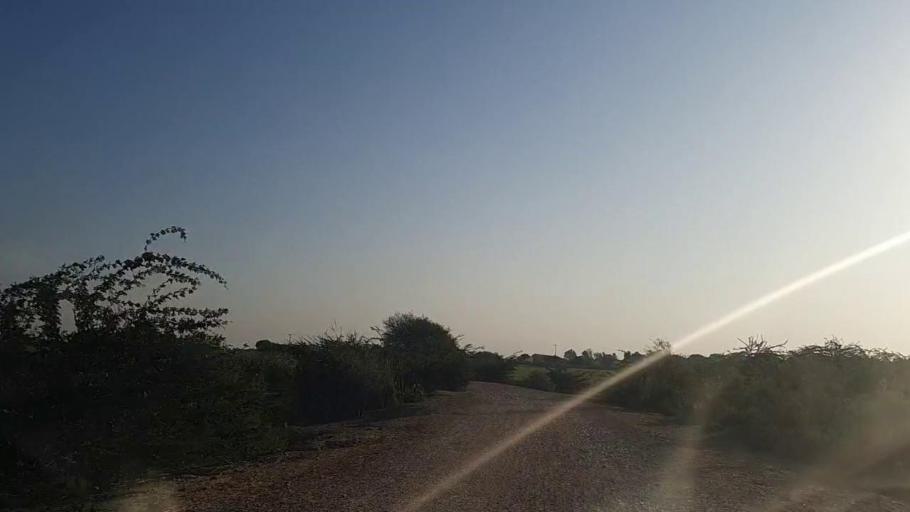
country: PK
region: Sindh
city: Jati
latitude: 24.4196
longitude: 68.1854
